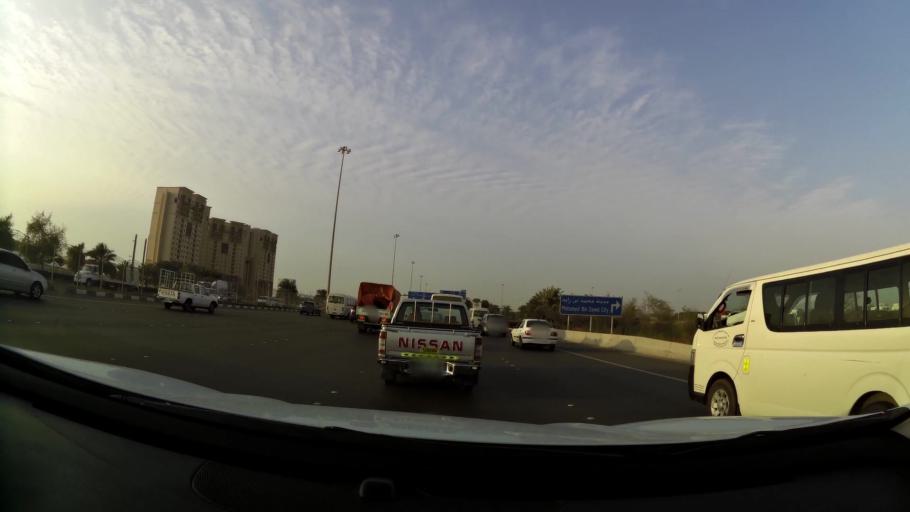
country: AE
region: Abu Dhabi
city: Abu Dhabi
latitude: 24.3814
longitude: 54.5248
